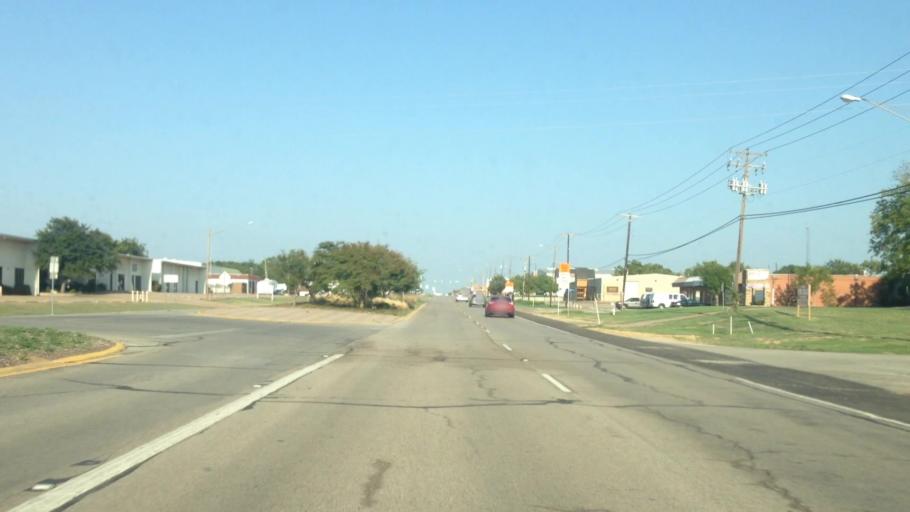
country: US
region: Texas
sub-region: Tarrant County
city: Richland Hills
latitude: 32.8092
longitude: -97.2426
